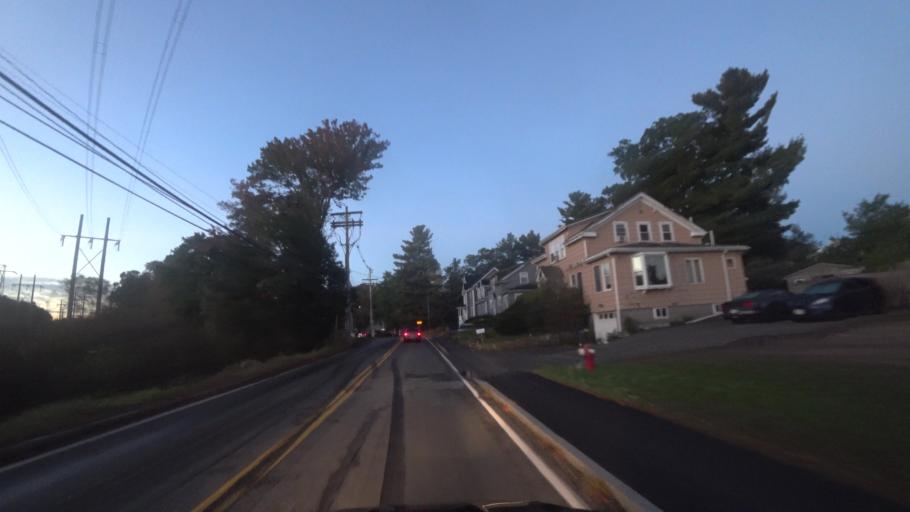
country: US
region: Massachusetts
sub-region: Essex County
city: Lynnfield
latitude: 42.5111
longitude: -71.0443
